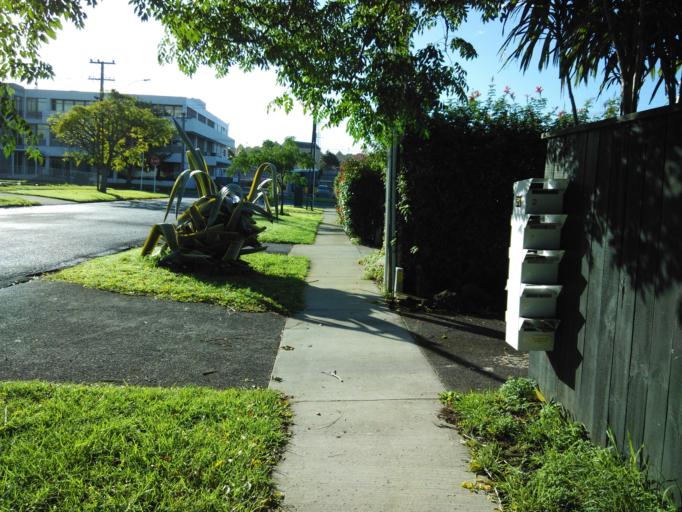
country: NZ
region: Auckland
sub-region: Auckland
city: Mangere
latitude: -36.9202
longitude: 174.7994
